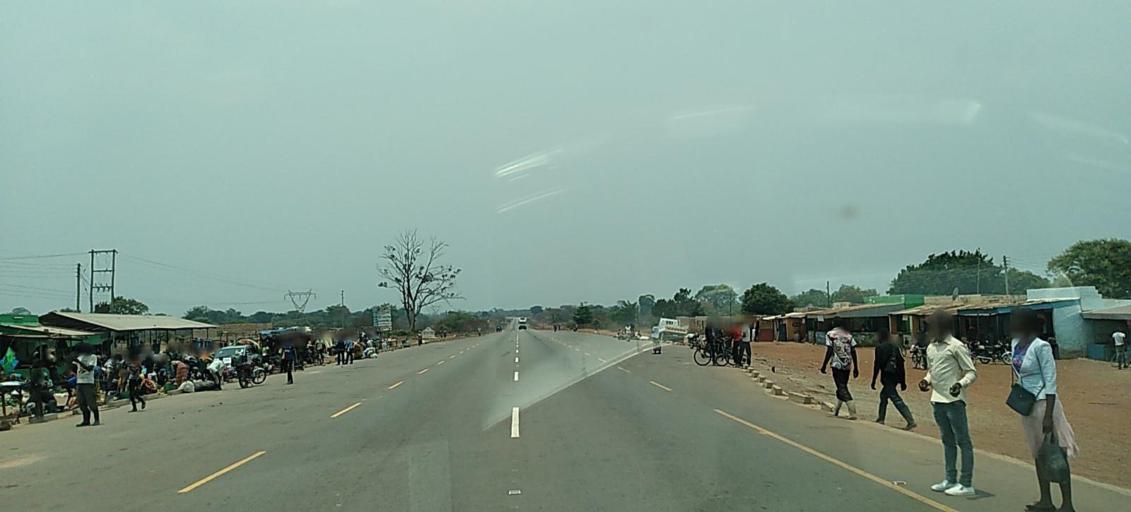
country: ZM
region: Copperbelt
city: Chililabombwe
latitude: -12.3808
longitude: 27.3213
